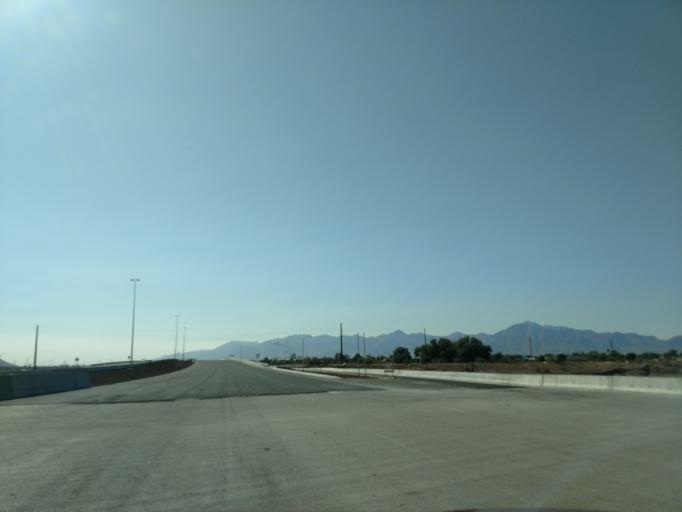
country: US
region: Arizona
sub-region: Maricopa County
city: Laveen
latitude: 33.3958
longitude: -112.1923
